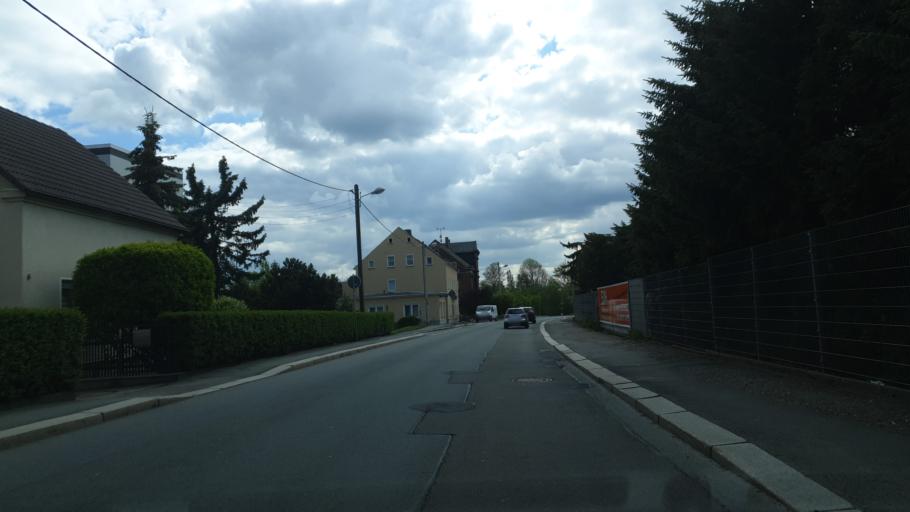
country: DE
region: Saxony
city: Lugau
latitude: 50.7434
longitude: 12.7507
